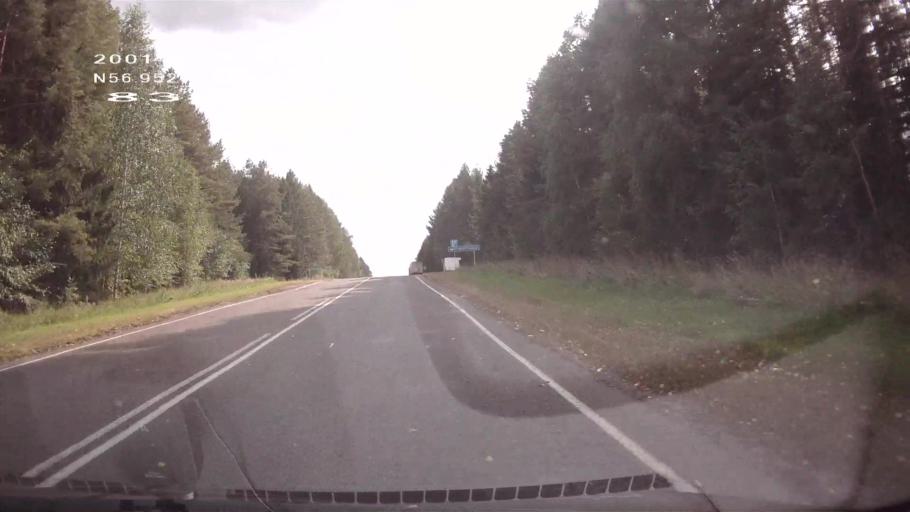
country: RU
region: Mariy-El
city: Kuzhener
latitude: 56.9517
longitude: 48.7502
